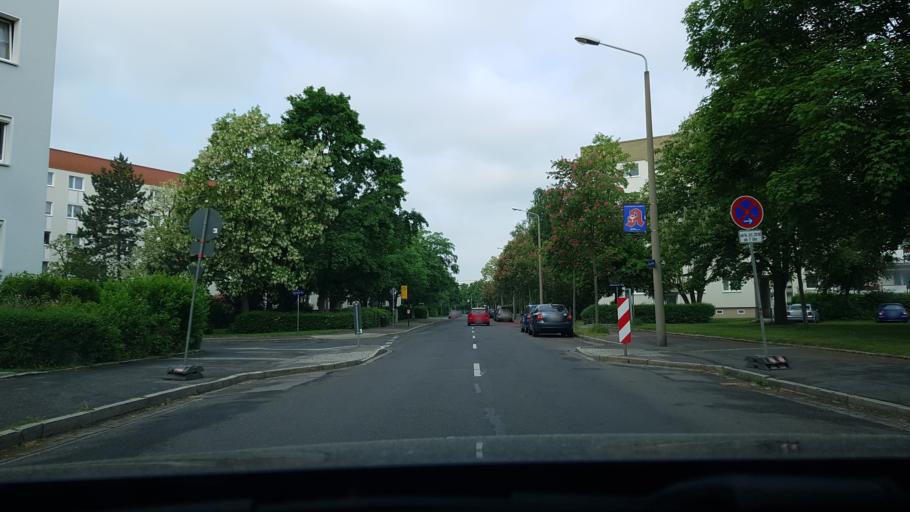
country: DE
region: Saxony
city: Heidenau
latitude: 51.0110
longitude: 13.8209
